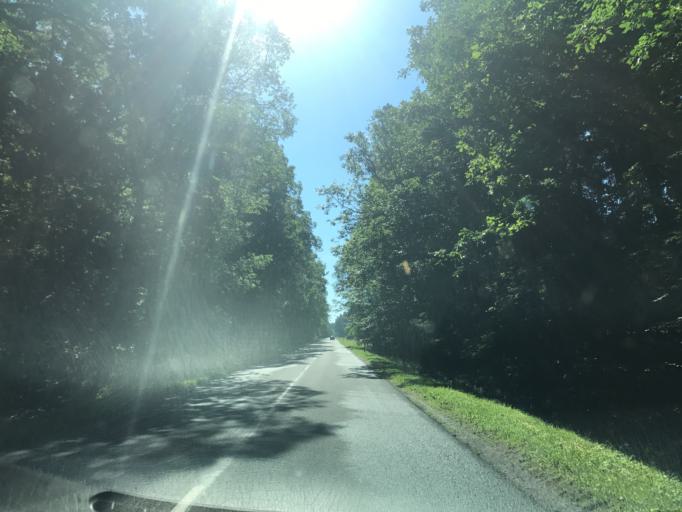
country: PL
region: Pomeranian Voivodeship
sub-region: Powiat slupski
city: Potegowo
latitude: 54.4042
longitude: 17.4518
